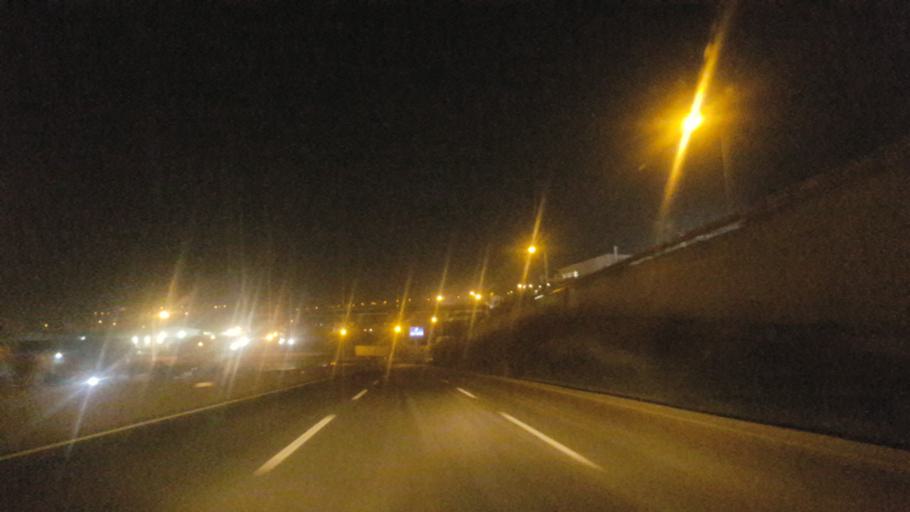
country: TR
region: Kocaeli
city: Tavsanli
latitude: 40.8007
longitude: 29.5265
